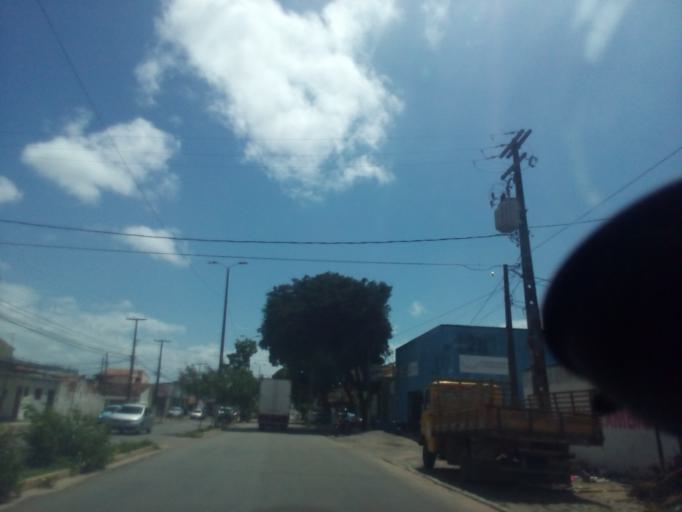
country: BR
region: Rio Grande do Norte
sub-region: Natal
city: Natal
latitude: -5.8234
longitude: -35.2336
